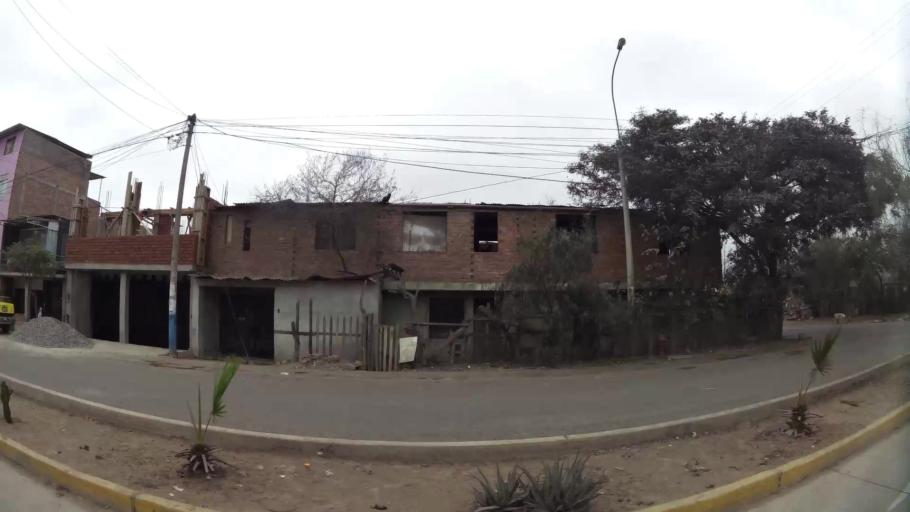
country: PE
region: Lima
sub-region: Lima
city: Surco
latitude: -12.1929
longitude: -76.9426
